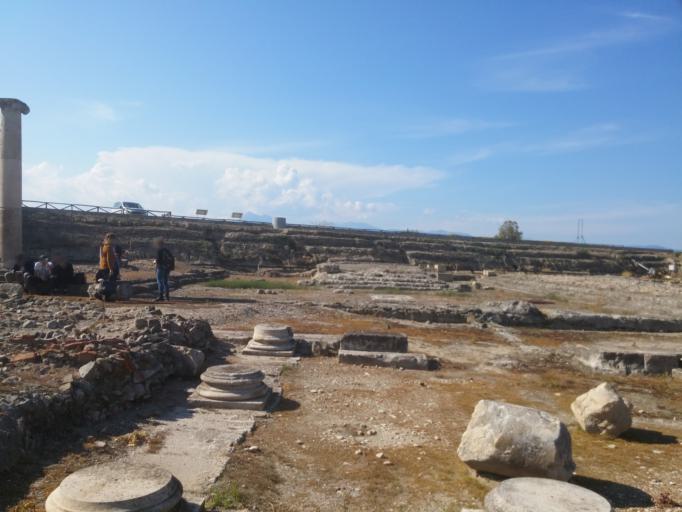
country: IT
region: Calabria
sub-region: Provincia di Cosenza
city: Sibari
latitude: 39.7181
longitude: 16.4975
